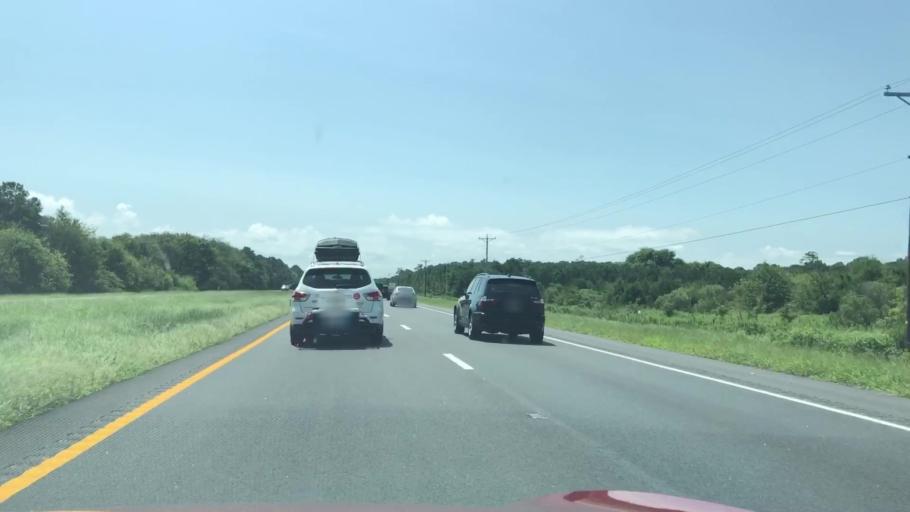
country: US
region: Virginia
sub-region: Northampton County
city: Cape Charles
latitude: 37.1626
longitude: -75.9706
